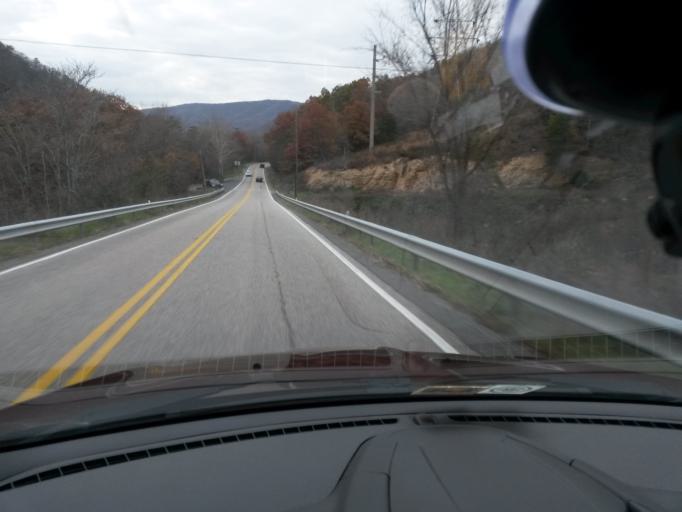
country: US
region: Virginia
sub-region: Rockbridge County
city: Glasgow
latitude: 37.6210
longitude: -79.4369
